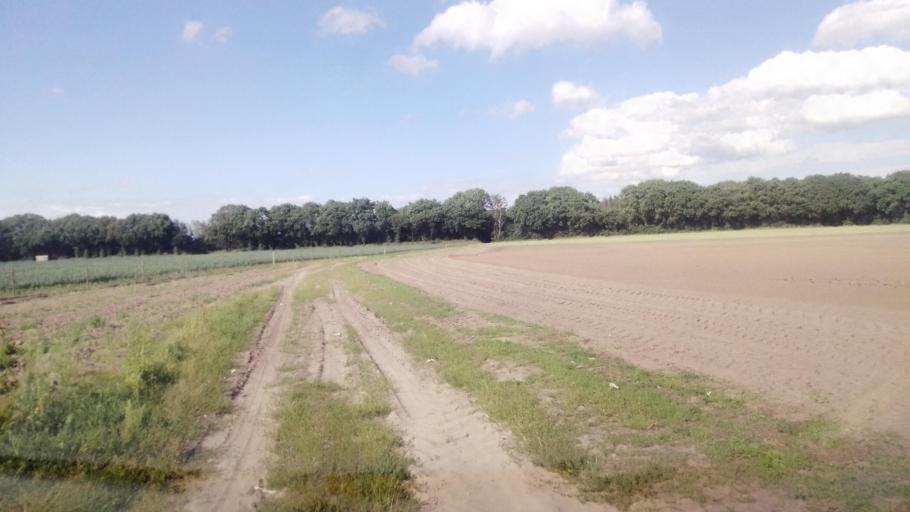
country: NL
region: Limburg
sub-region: Gemeente Peel en Maas
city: Maasbree
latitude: 51.3721
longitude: 6.0815
